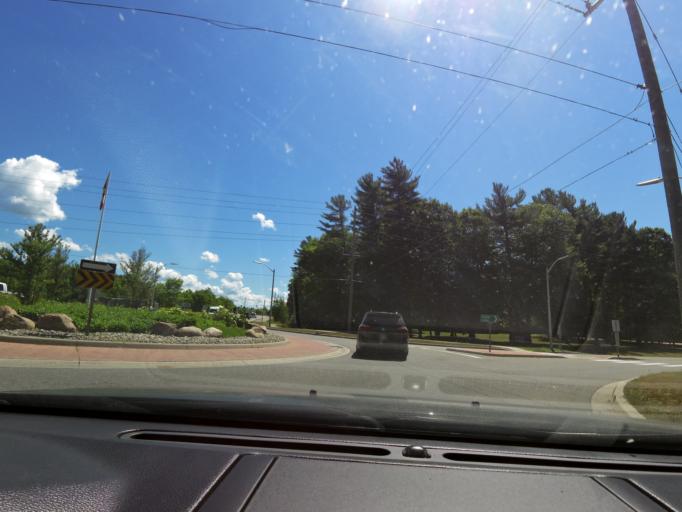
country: CA
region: Ontario
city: Bracebridge
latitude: 45.0505
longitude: -79.2961
